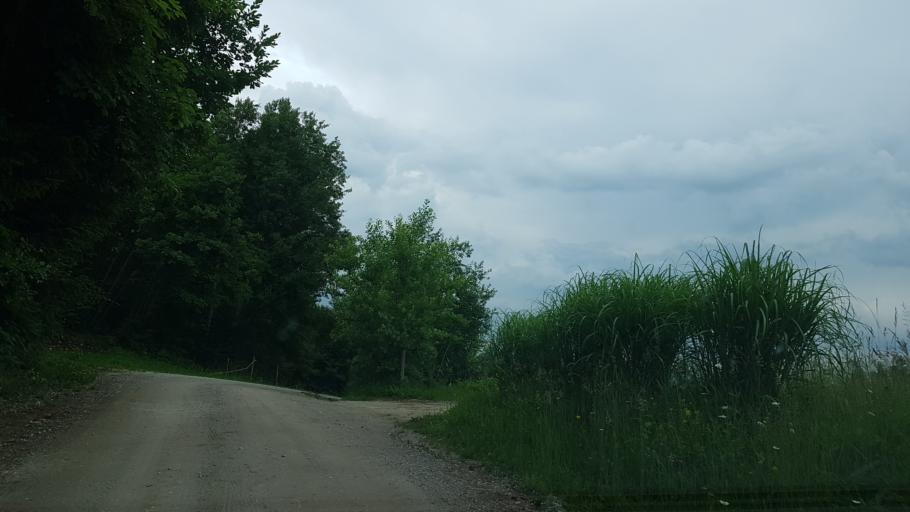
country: SI
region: Dobrna
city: Dobrna
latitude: 46.3637
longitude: 15.2455
